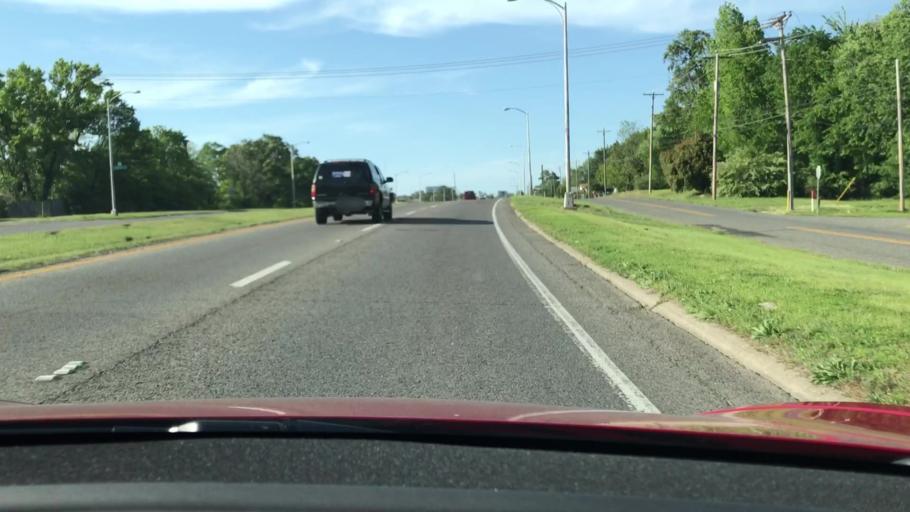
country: US
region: Louisiana
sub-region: Bossier Parish
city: Bossier City
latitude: 32.4942
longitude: -93.7247
